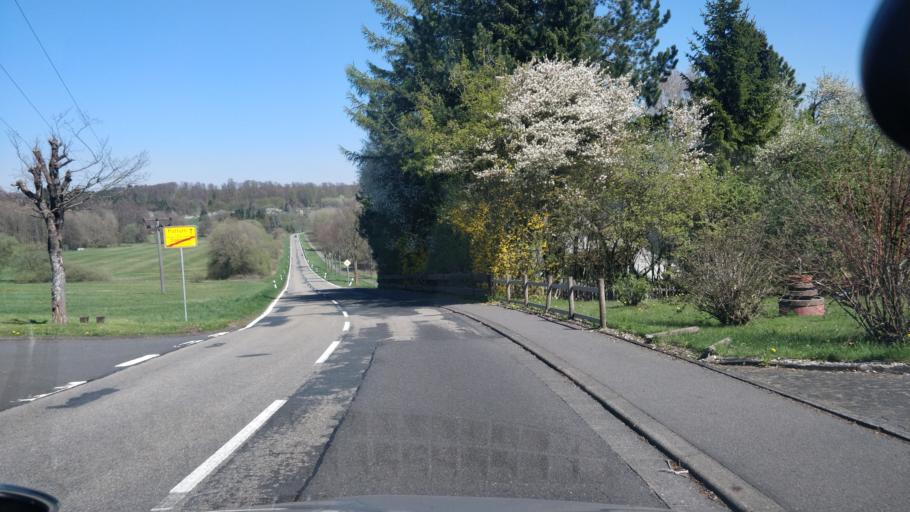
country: DE
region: Rheinland-Pfalz
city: Pottum
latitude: 50.5875
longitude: 7.9893
